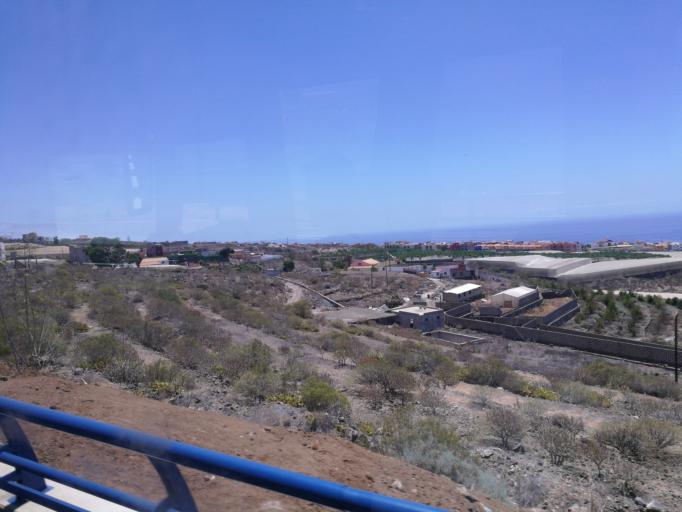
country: ES
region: Canary Islands
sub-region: Provincia de Santa Cruz de Tenerife
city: Guia de Isora
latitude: 28.1857
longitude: -16.7884
